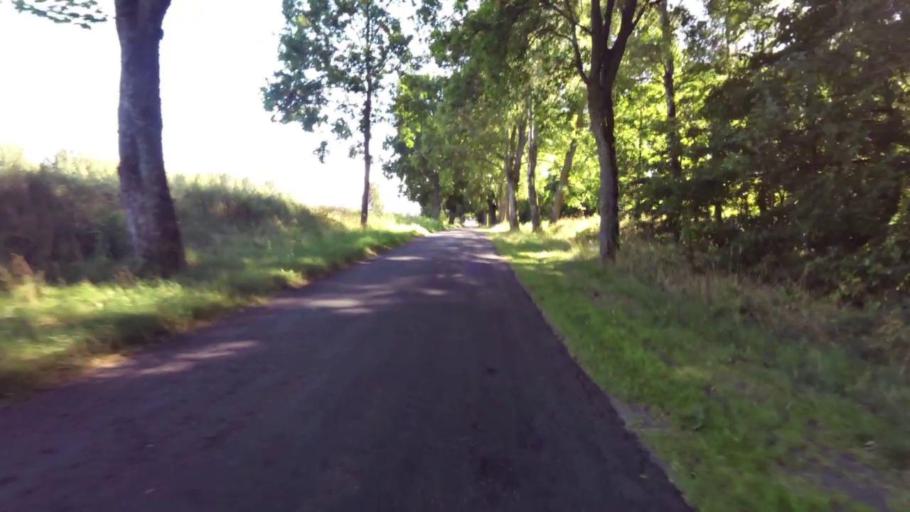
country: PL
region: West Pomeranian Voivodeship
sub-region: Powiat szczecinecki
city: Szczecinek
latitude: 53.7800
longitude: 16.6772
